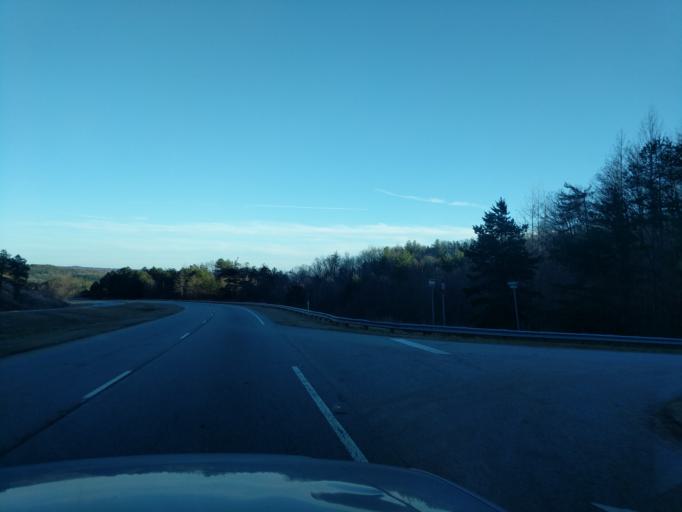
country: US
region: Georgia
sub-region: Stephens County
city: Toccoa
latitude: 34.5549
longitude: -83.3826
